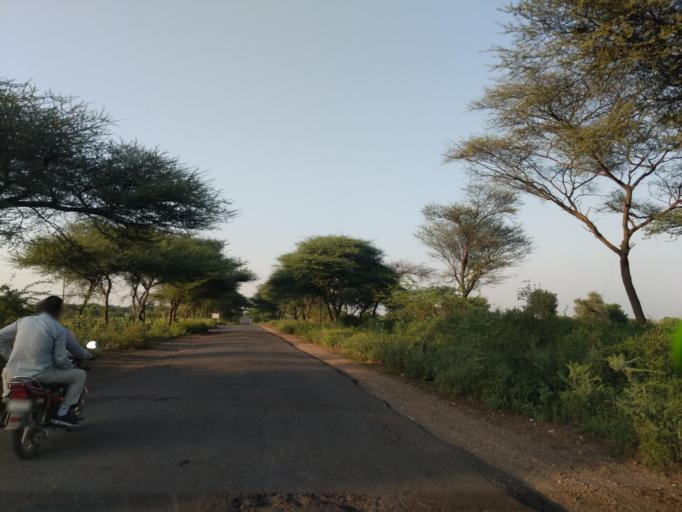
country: IN
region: Rajasthan
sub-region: Churu
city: Rajgarh
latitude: 28.6101
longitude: 75.3773
